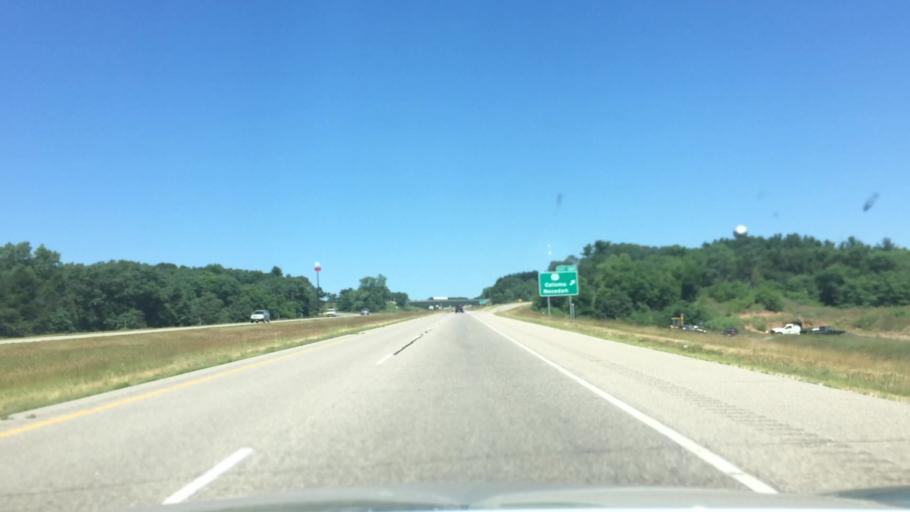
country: US
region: Wisconsin
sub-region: Marquette County
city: Westfield
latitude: 44.0299
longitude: -89.5238
